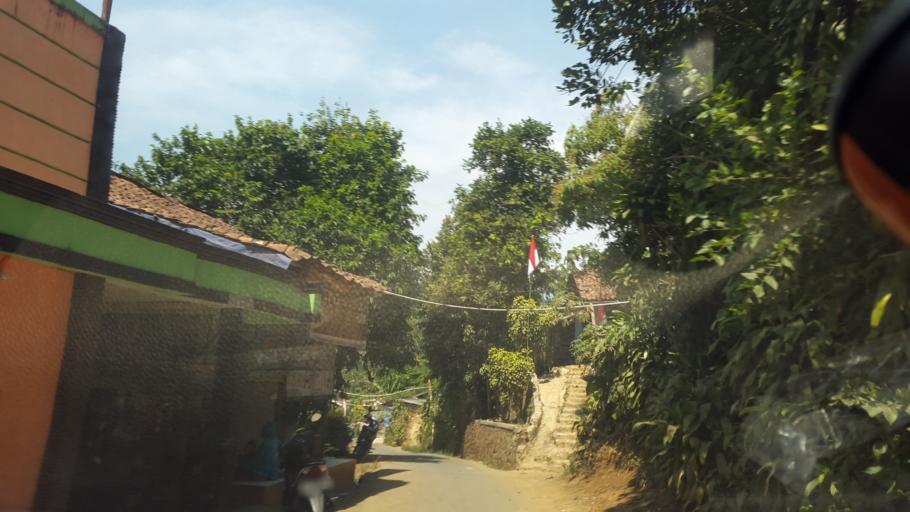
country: ID
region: West Java
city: Sindangsari
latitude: -6.8991
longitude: 106.6487
